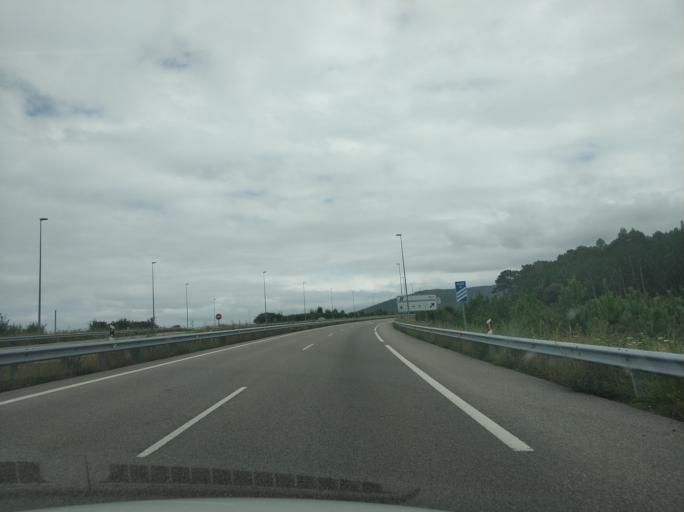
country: ES
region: Asturias
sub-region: Province of Asturias
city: Cudillero
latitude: 43.5573
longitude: -6.1741
